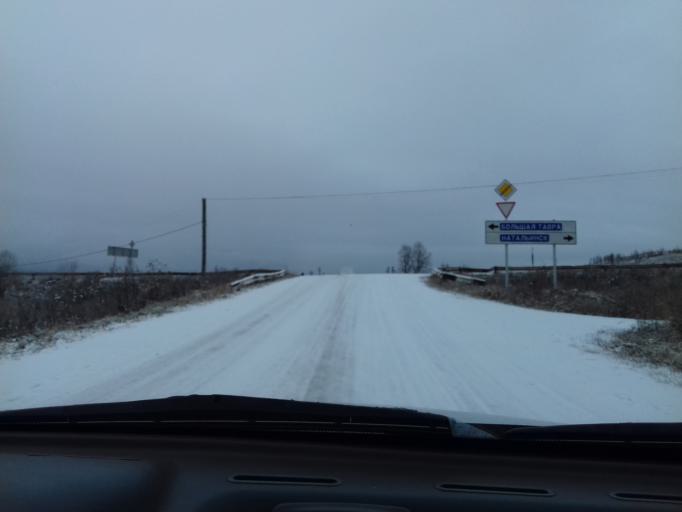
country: RU
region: Sverdlovsk
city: Sarana
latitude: 56.3005
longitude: 57.9575
